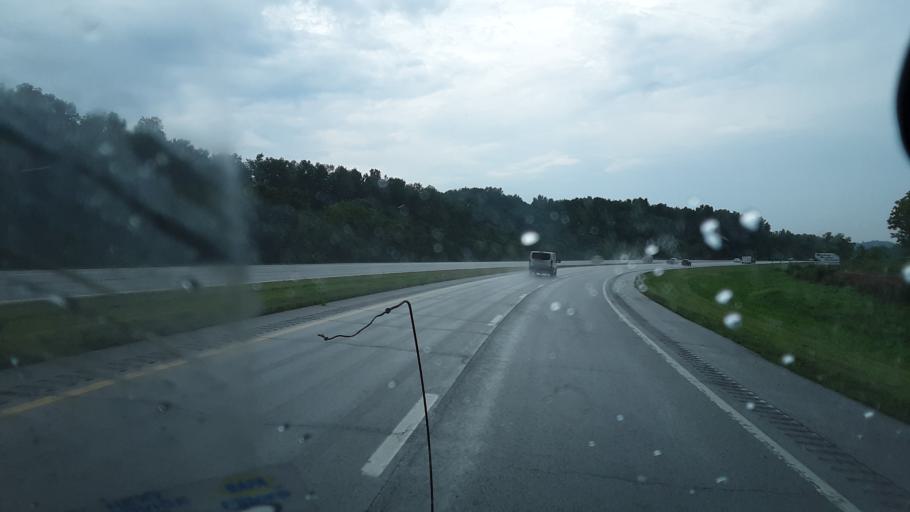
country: US
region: Ohio
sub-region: Hocking County
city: Logan
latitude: 39.5038
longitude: -82.3543
